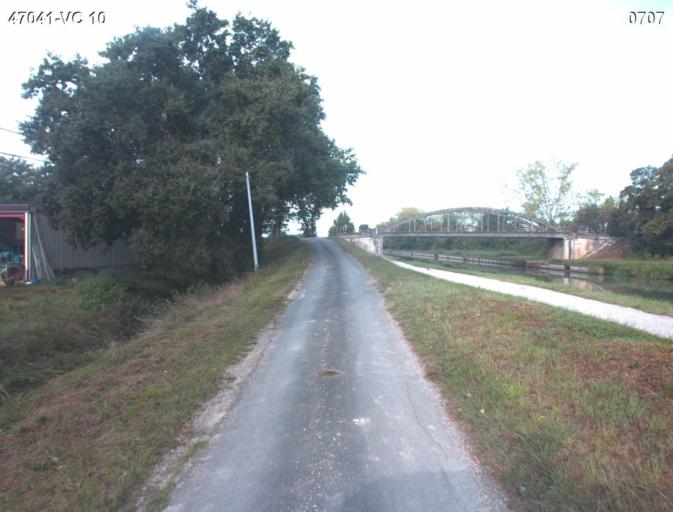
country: FR
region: Aquitaine
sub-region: Departement du Lot-et-Garonne
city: Port-Sainte-Marie
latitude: 44.2179
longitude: 0.4254
